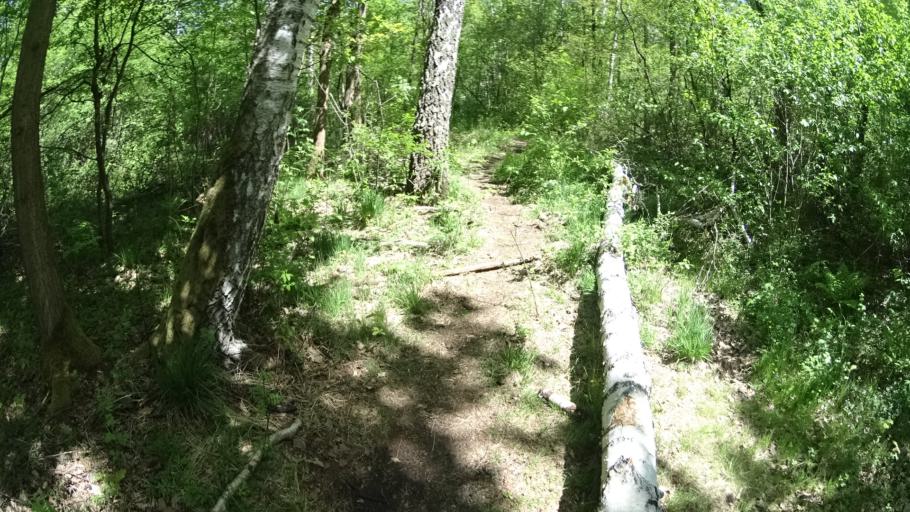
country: PL
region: Masovian Voivodeship
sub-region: Warszawa
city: Bemowo
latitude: 52.2700
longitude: 20.8833
